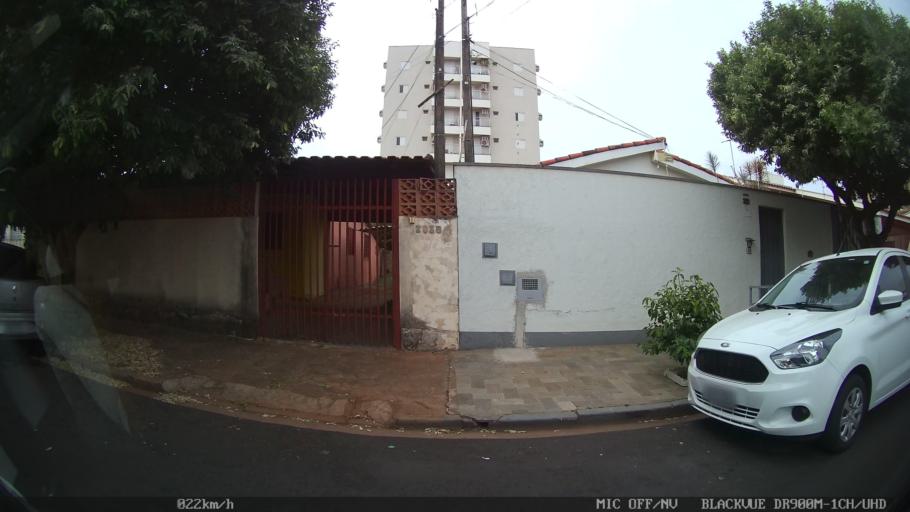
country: BR
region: Sao Paulo
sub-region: Sao Jose Do Rio Preto
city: Sao Jose do Rio Preto
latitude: -20.8353
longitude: -49.3898
